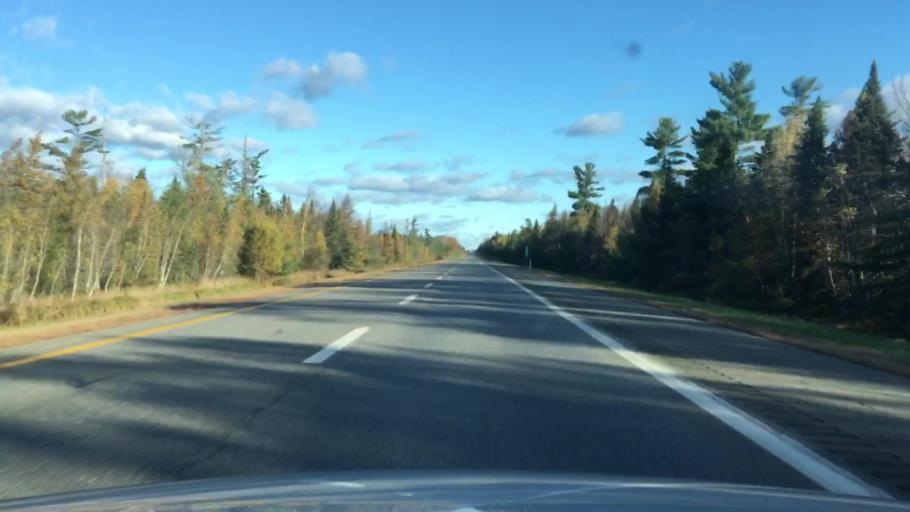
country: US
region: Maine
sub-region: Penobscot County
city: Greenbush
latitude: 45.0582
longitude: -68.6880
